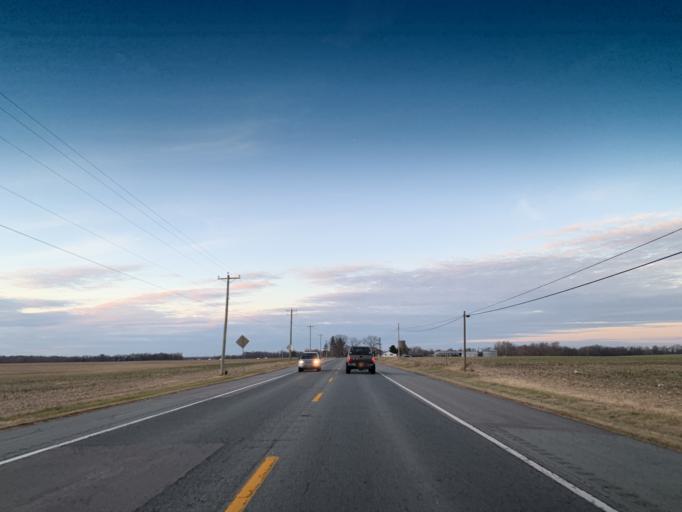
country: US
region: Delaware
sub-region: New Castle County
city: Middletown
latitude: 39.4344
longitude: -75.8613
